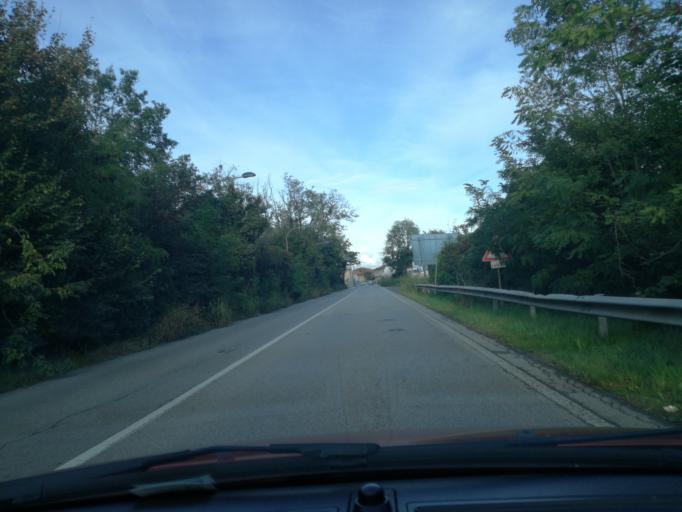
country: IT
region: Lombardy
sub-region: Provincia di Monza e Brianza
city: Vimercate
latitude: 45.6088
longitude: 9.3751
